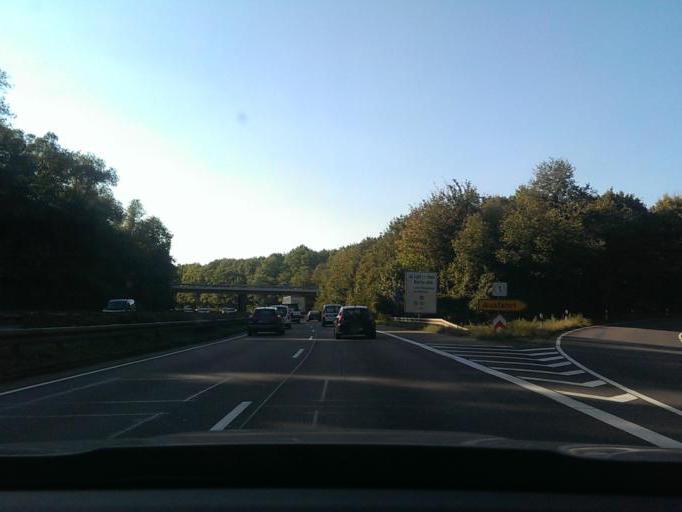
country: DE
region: Baden-Wuerttemberg
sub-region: Karlsruhe Region
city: Karlsruhe
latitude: 48.9944
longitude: 8.4288
